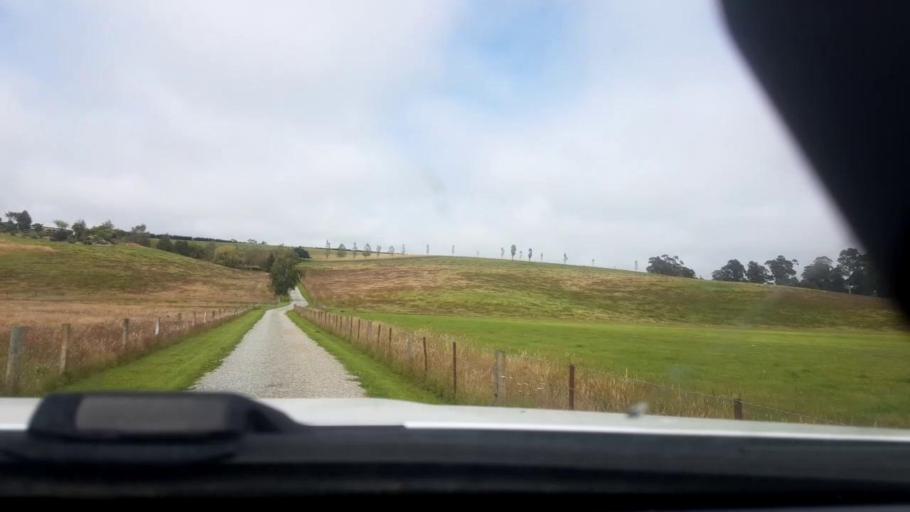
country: NZ
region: Canterbury
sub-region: Timaru District
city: Pleasant Point
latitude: -44.3222
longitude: 171.1913
